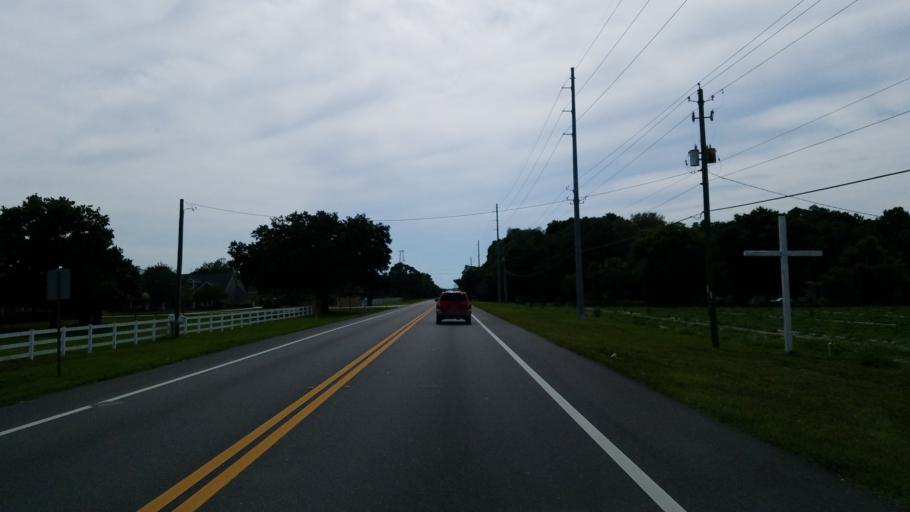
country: US
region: Florida
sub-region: Hillsborough County
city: Fish Hawk
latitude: 27.8501
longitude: -82.1654
